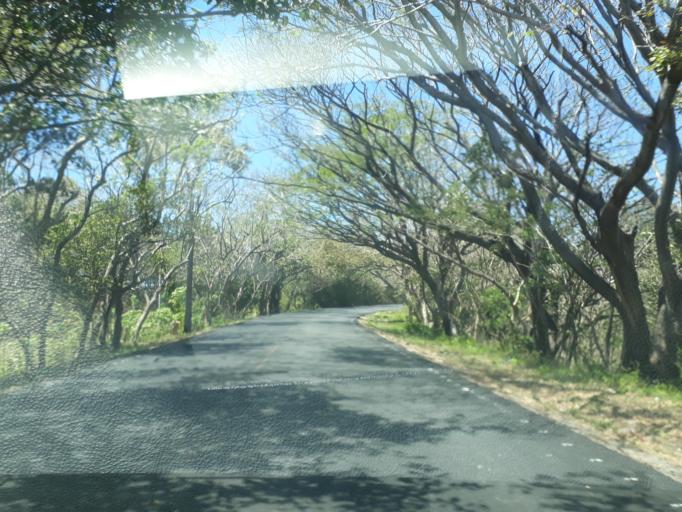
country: CR
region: Guanacaste
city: La Cruz
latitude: 10.8490
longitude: -85.5710
